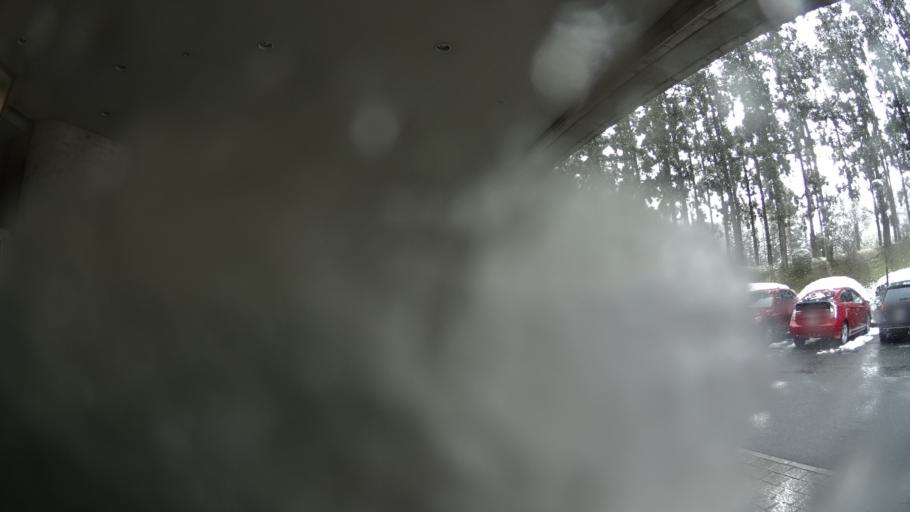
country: JP
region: Kyoto
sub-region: Kyoto-shi
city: Kamigyo-ku
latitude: 35.0627
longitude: 135.7807
